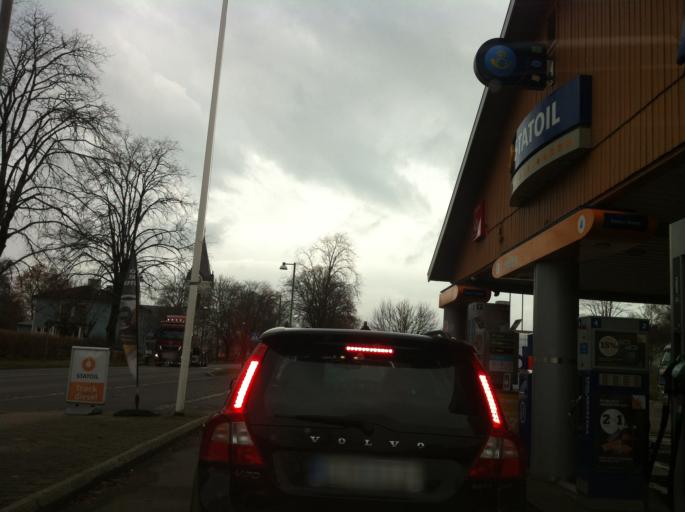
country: SE
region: Joenkoeping
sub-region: Savsjo Kommun
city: Vrigstad
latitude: 57.3586
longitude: 14.4856
